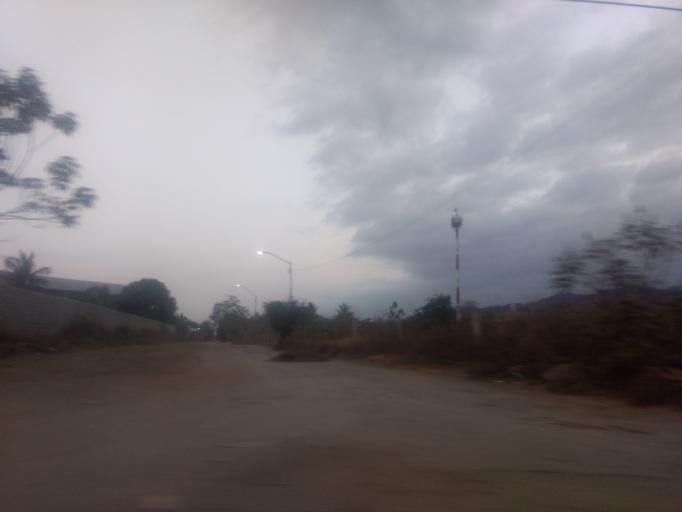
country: MX
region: Colima
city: Tapeixtles
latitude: 19.0890
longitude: -104.2921
